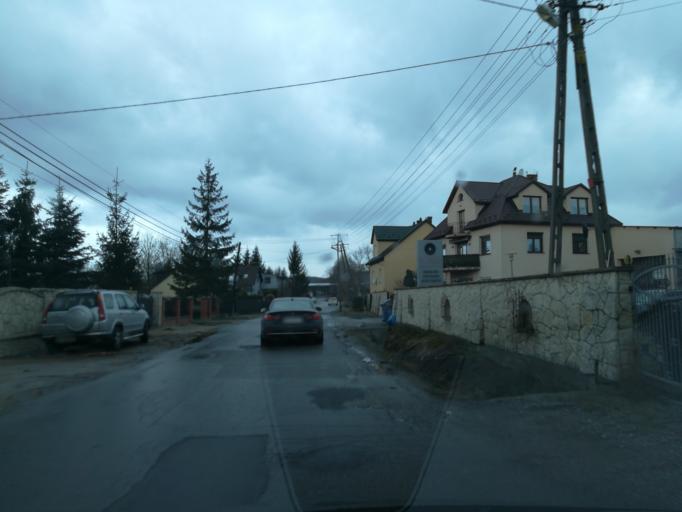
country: PL
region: Lesser Poland Voivodeship
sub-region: Krakow
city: Sidzina
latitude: 49.9946
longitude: 19.8560
